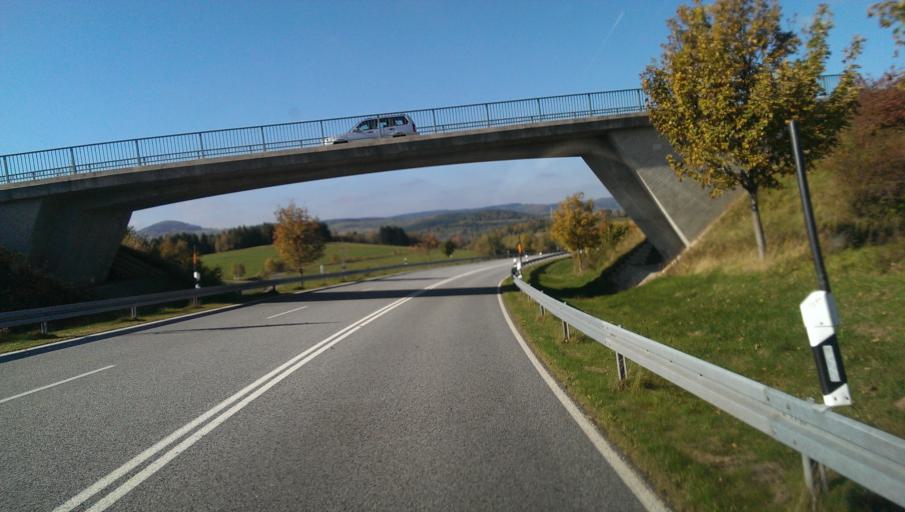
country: DE
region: Saxony
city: Barenstein
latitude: 50.7808
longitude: 13.8472
